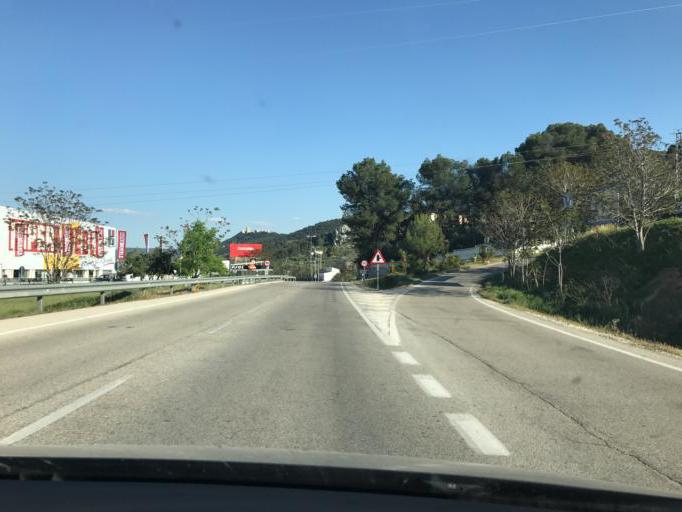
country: ES
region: Andalusia
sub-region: Provincia de Jaen
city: Jaen
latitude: 37.7854
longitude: -3.8281
